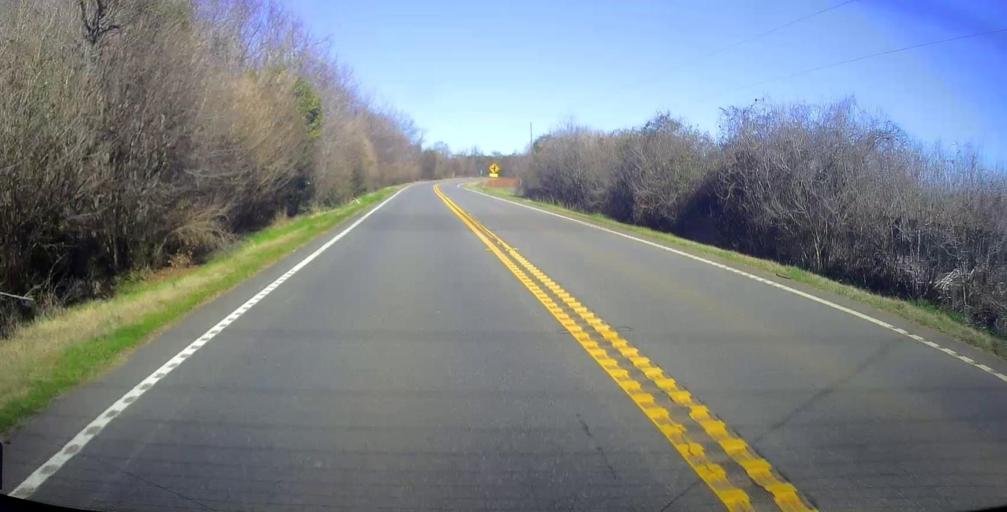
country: US
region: Georgia
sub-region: Macon County
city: Marshallville
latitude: 32.4472
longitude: -83.9830
